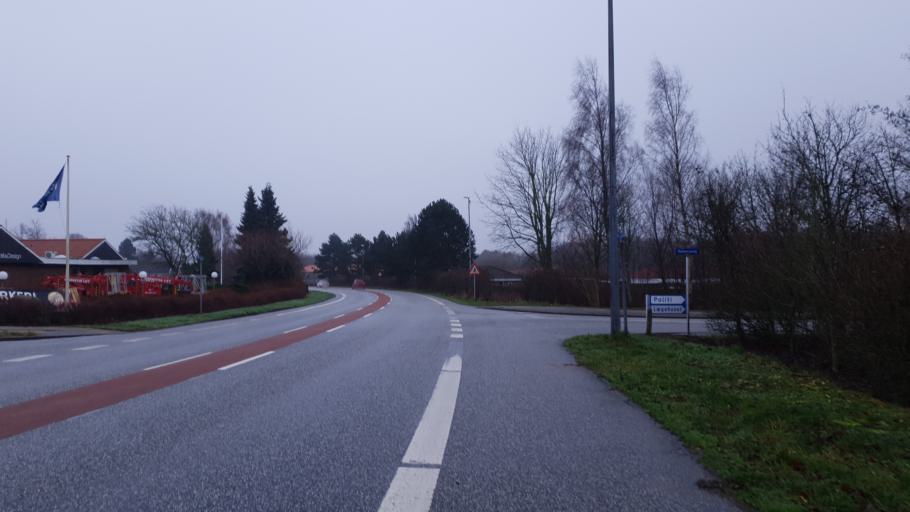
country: DK
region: Central Jutland
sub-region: Hedensted Kommune
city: Hedensted
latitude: 55.7776
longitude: 9.6959
